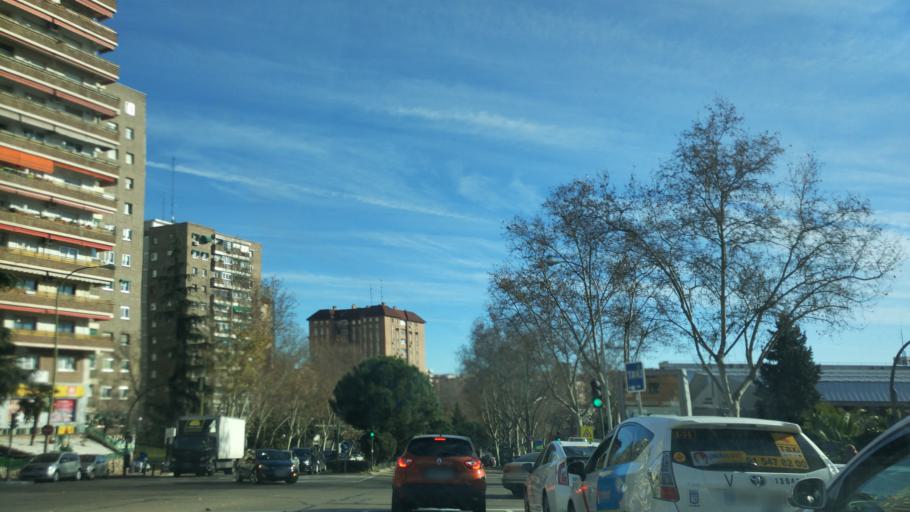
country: ES
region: Madrid
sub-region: Provincia de Madrid
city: Tetuan de las Victorias
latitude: 40.4842
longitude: -3.7075
